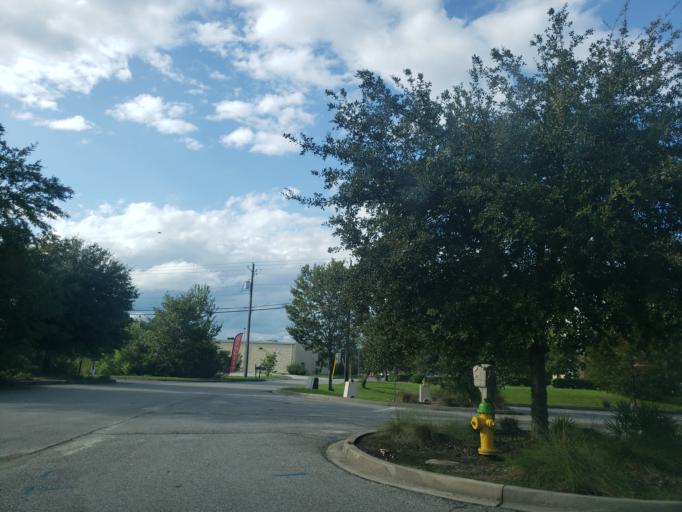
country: US
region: Georgia
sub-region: Chatham County
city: Georgetown
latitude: 31.9963
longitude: -81.2565
